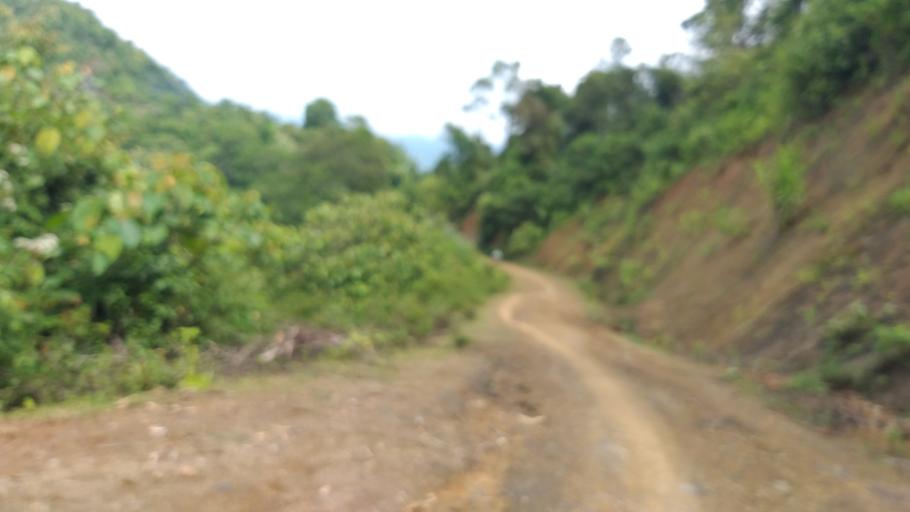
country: VN
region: Huyen Dien Bien
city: Dien Bien Phu
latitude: 21.4295
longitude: 102.6794
